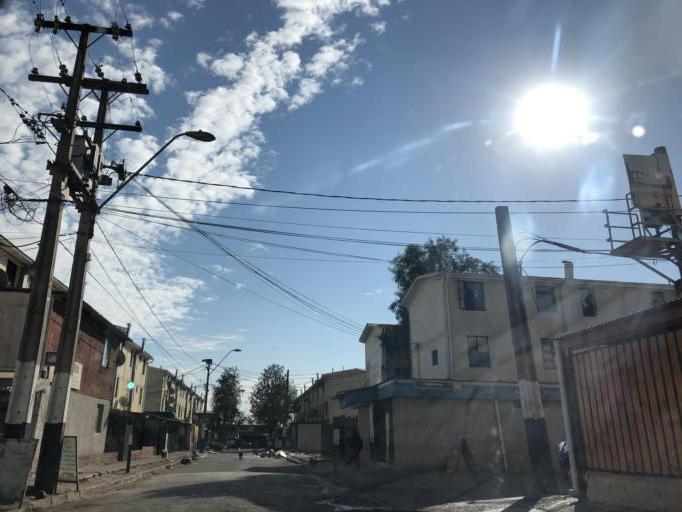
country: CL
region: Santiago Metropolitan
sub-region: Provincia de Santiago
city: La Pintana
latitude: -33.6282
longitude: -70.6220
